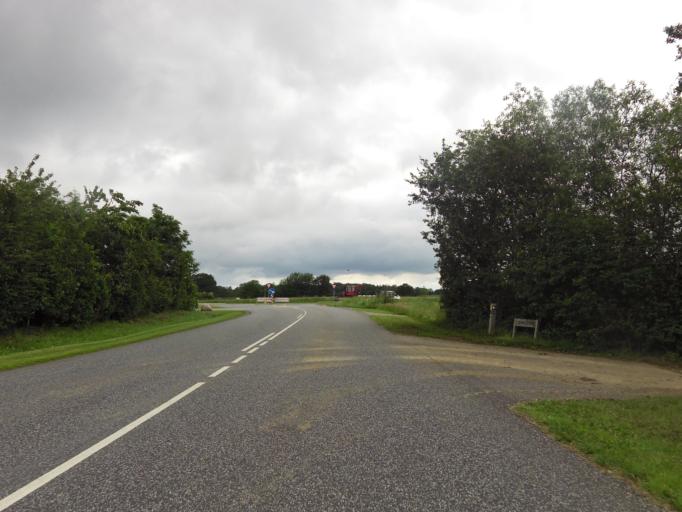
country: DK
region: South Denmark
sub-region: Tonder Kommune
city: Toftlund
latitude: 55.1214
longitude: 9.0752
